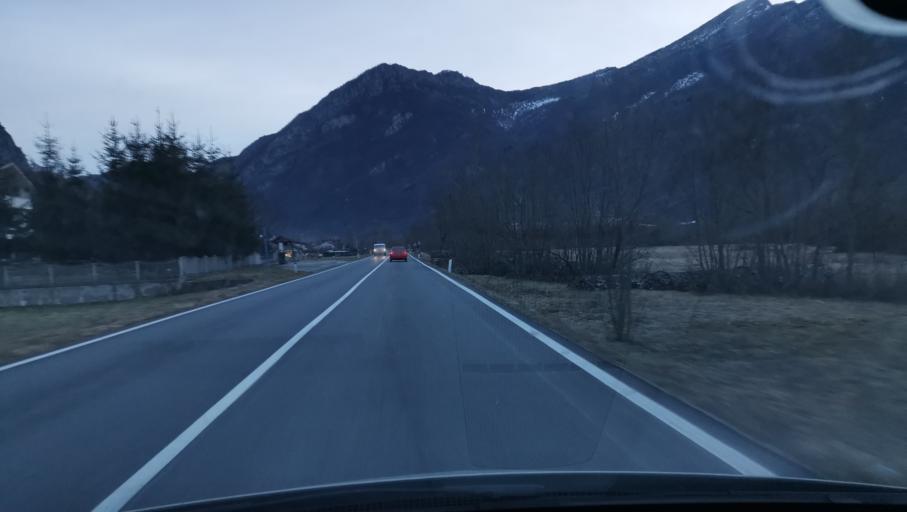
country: IT
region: Piedmont
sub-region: Provincia di Cuneo
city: Moiola
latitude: 44.3106
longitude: 7.3632
